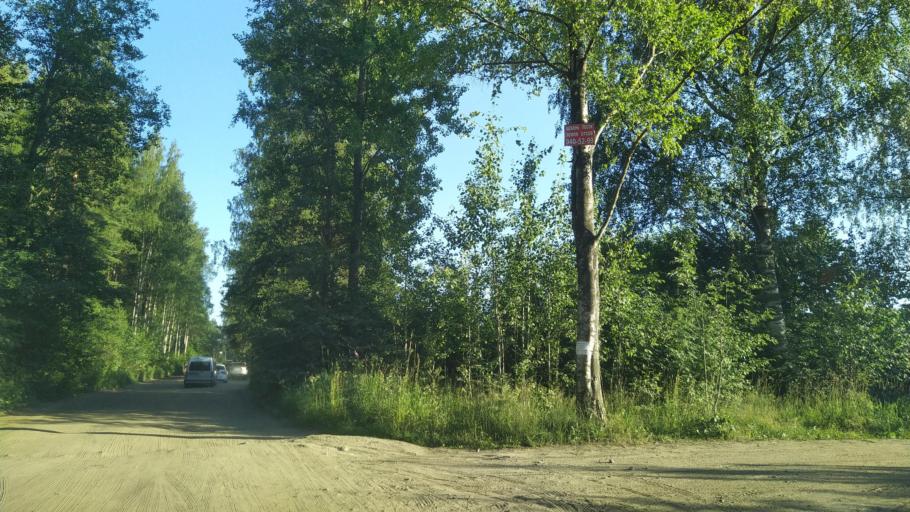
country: RU
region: Leningrad
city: Koltushi
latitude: 59.9156
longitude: 30.7348
